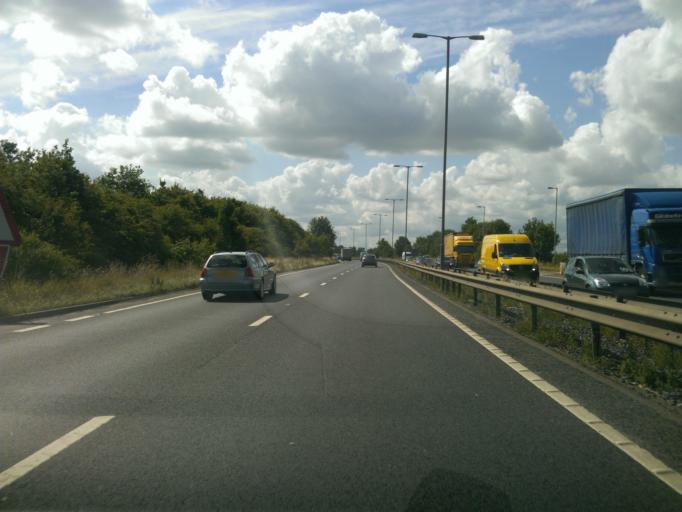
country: GB
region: England
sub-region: Northamptonshire
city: Rothwell
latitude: 52.4128
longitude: -0.7695
